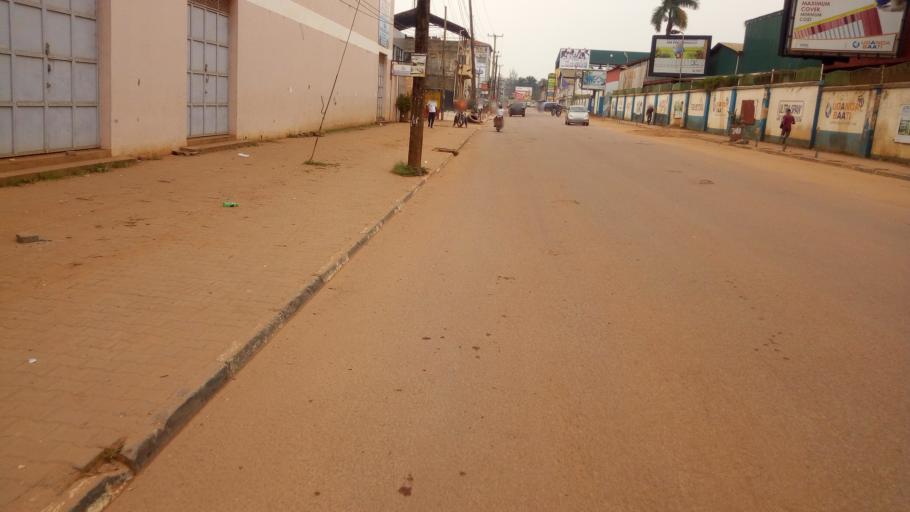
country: UG
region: Central Region
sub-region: Kampala District
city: Kampala
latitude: 0.3141
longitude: 32.6142
